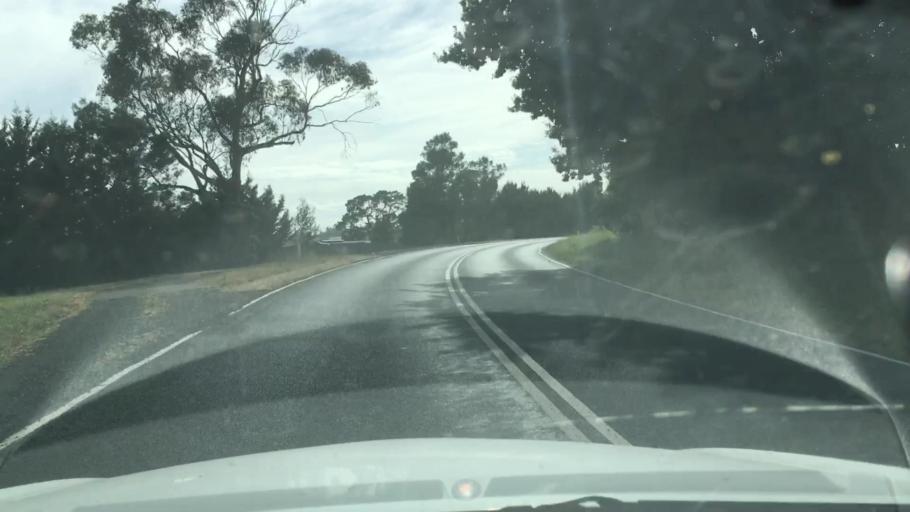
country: AU
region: Victoria
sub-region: Yarra Ranges
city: Woori Yallock
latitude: -37.8061
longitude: 145.5186
